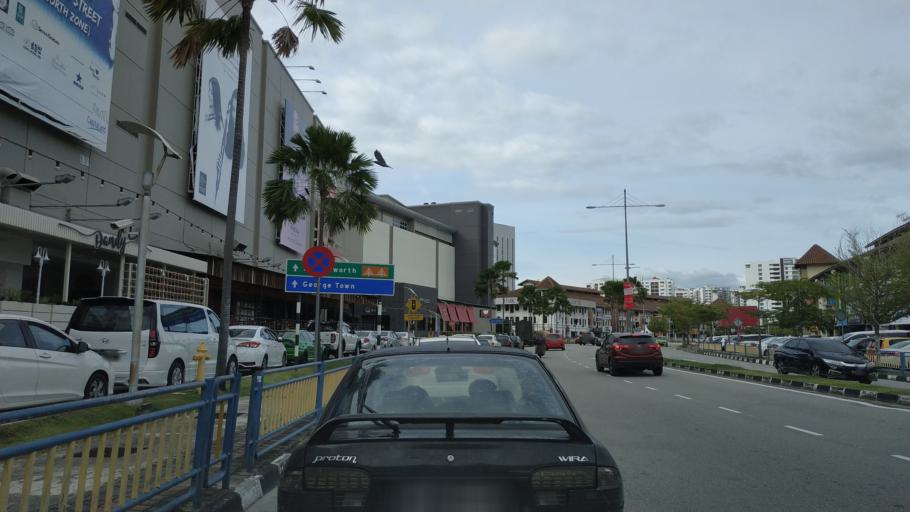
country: MY
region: Penang
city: Kampung Sungai Ara
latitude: 5.3338
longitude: 100.3070
